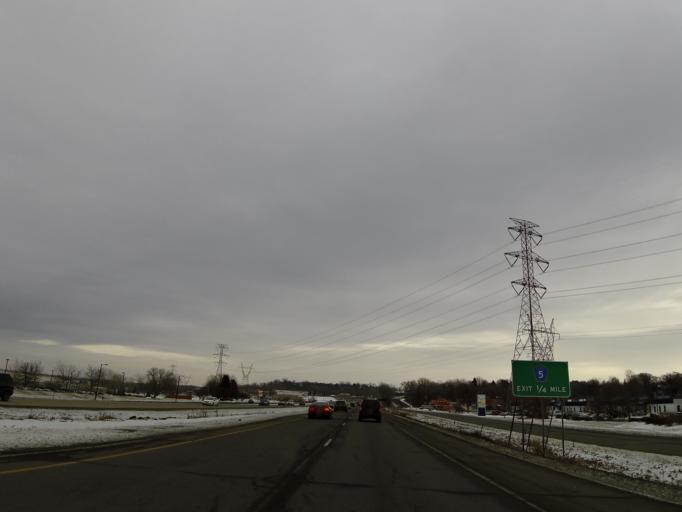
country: US
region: Minnesota
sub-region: Scott County
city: Savage
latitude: 44.7749
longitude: -93.3148
